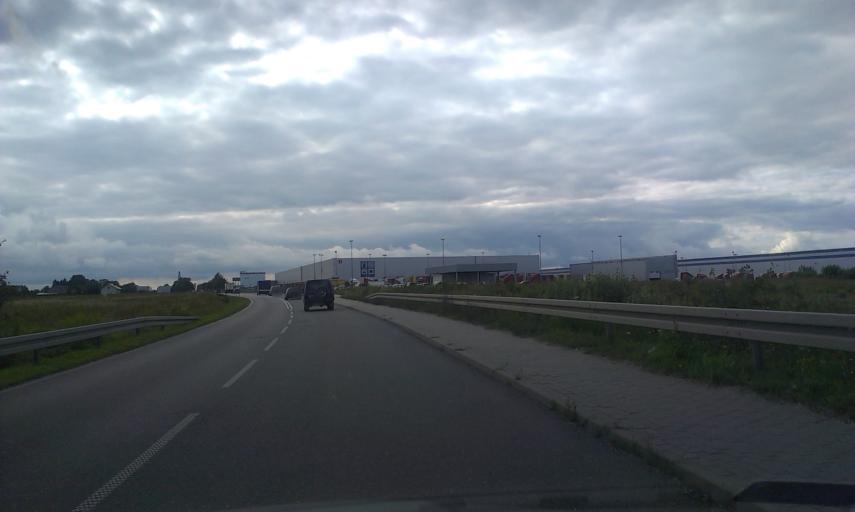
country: PL
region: Masovian Voivodeship
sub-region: Powiat zyrardowski
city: Radziejowice
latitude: 51.9724
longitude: 20.5668
